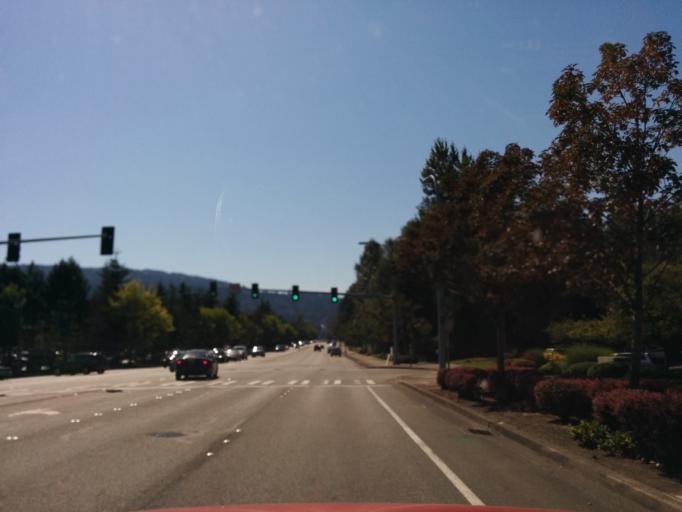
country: US
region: Washington
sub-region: King County
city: Issaquah
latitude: 47.5520
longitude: -122.0494
